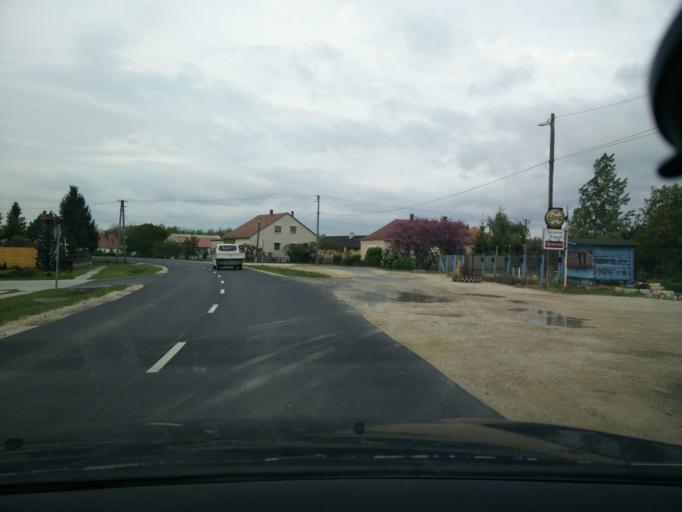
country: HU
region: Gyor-Moson-Sopron
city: Tet
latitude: 47.4668
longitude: 17.4922
